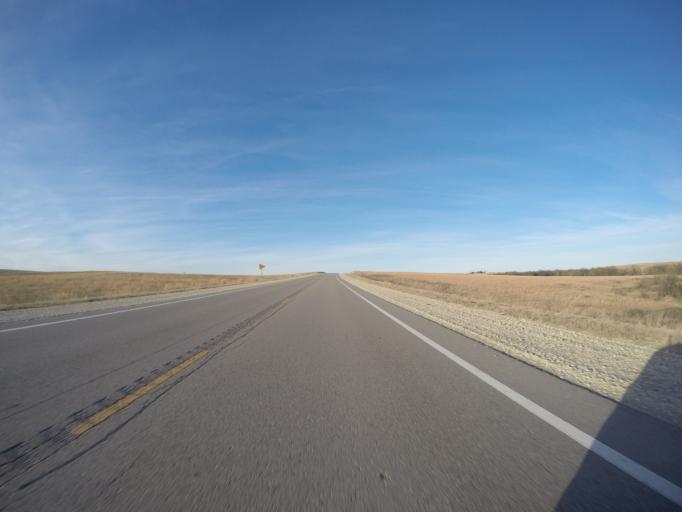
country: US
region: Kansas
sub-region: Marion County
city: Marion
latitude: 38.2961
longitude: -96.9664
